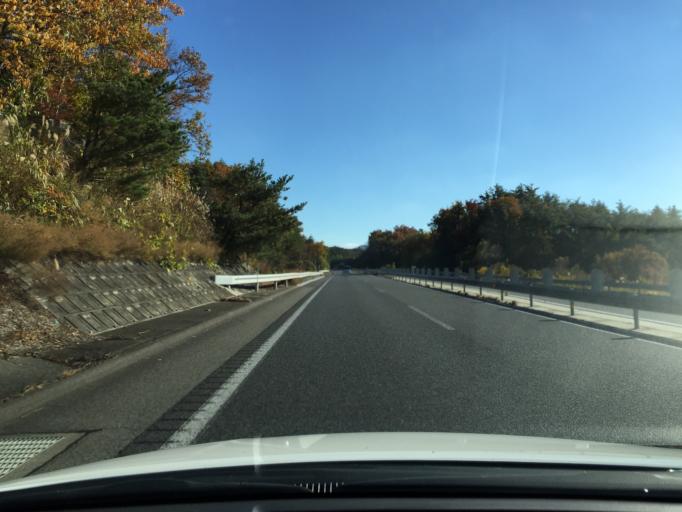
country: JP
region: Fukushima
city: Funehikimachi-funehiki
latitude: 37.4181
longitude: 140.5607
